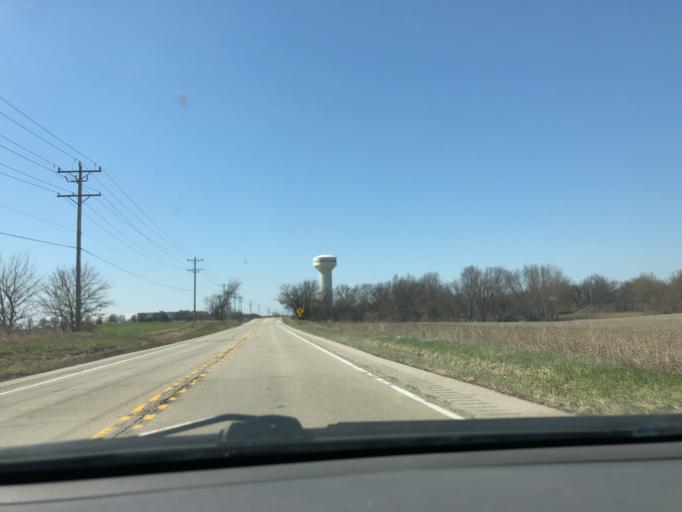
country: US
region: Illinois
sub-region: Kane County
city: Hampshire
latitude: 42.1335
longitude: -88.4967
